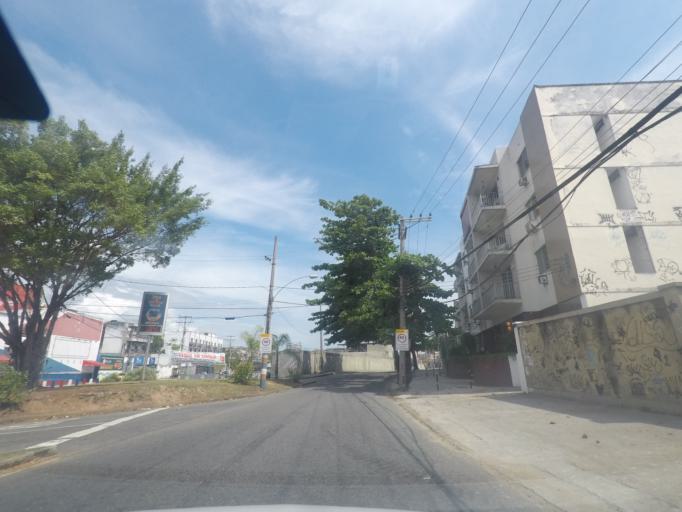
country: BR
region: Rio de Janeiro
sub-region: Rio De Janeiro
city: Rio de Janeiro
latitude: -22.8139
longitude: -43.1896
